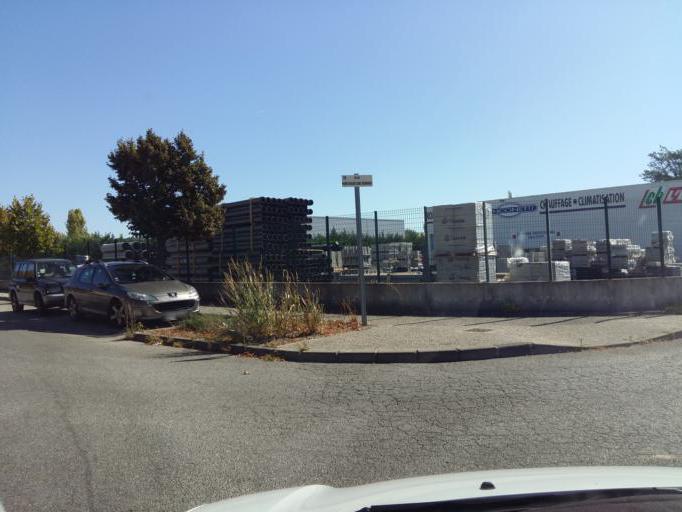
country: FR
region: Provence-Alpes-Cote d'Azur
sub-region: Departement du Vaucluse
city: Cadenet
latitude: 43.7280
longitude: 5.3699
